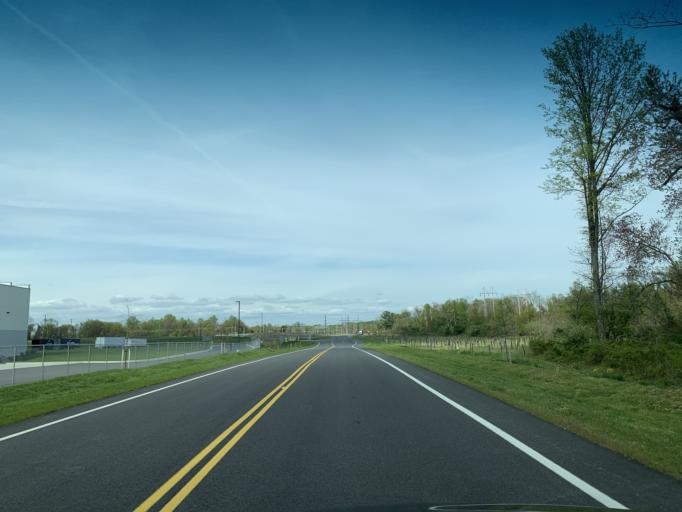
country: US
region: Maryland
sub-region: Harford County
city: Aberdeen
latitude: 39.4844
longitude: -76.1773
